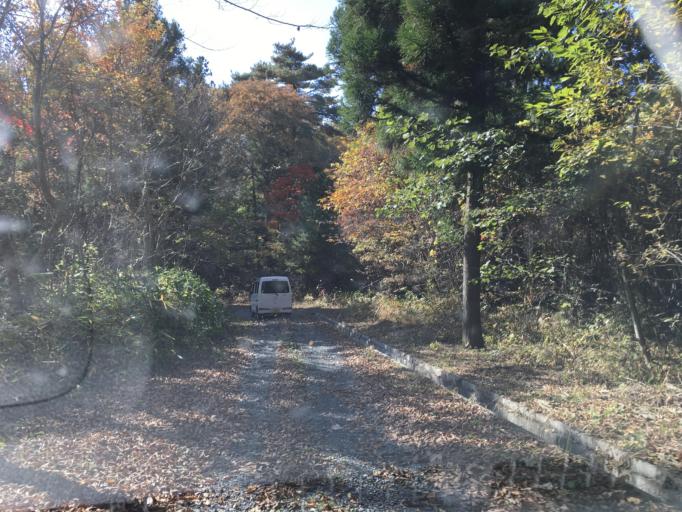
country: JP
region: Iwate
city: Ichinoseki
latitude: 38.9655
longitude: 141.4167
